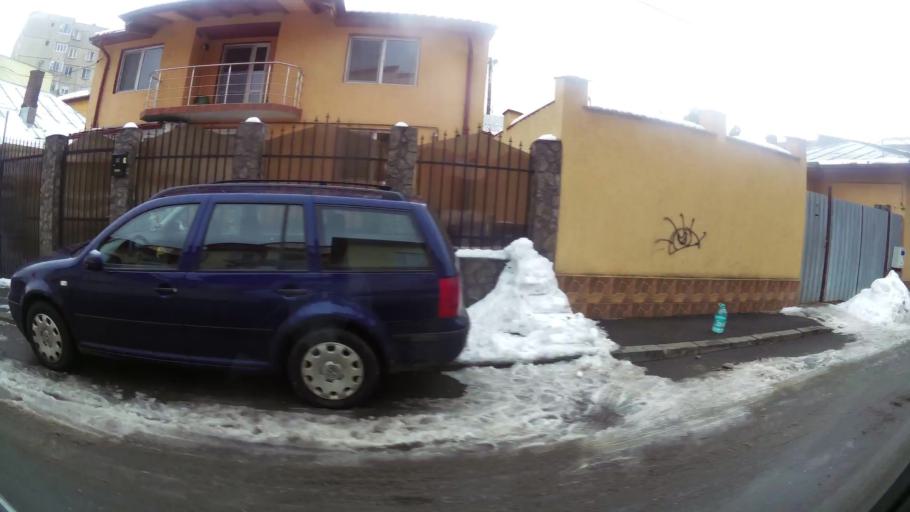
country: RO
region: Bucuresti
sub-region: Municipiul Bucuresti
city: Bucuresti
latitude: 44.4121
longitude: 26.0657
